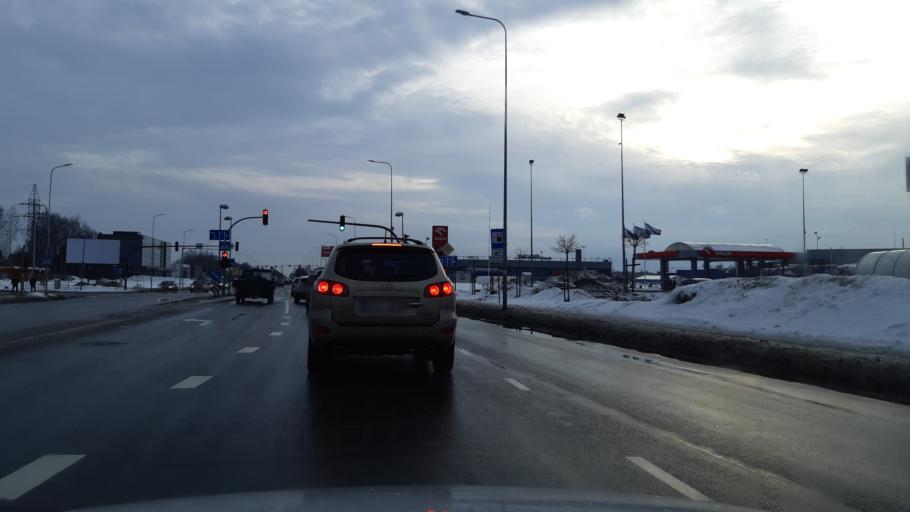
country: LT
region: Kauno apskritis
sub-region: Kaunas
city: Aleksotas
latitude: 54.8680
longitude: 23.8887
